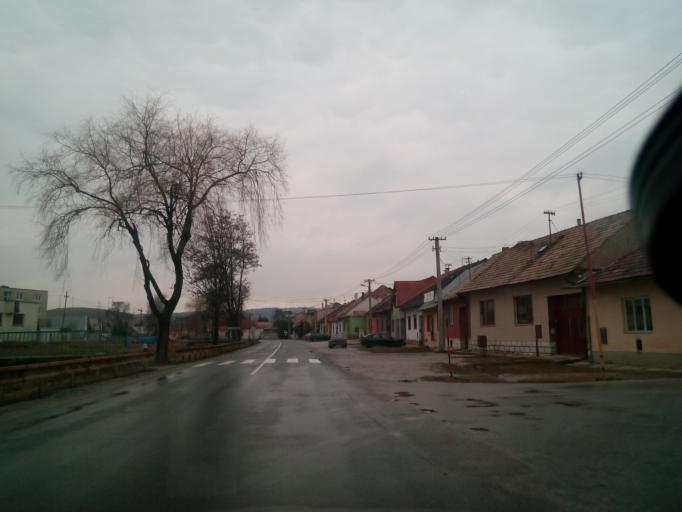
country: SK
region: Presovsky
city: Spisske Podhradie
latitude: 48.9500
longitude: 20.7973
